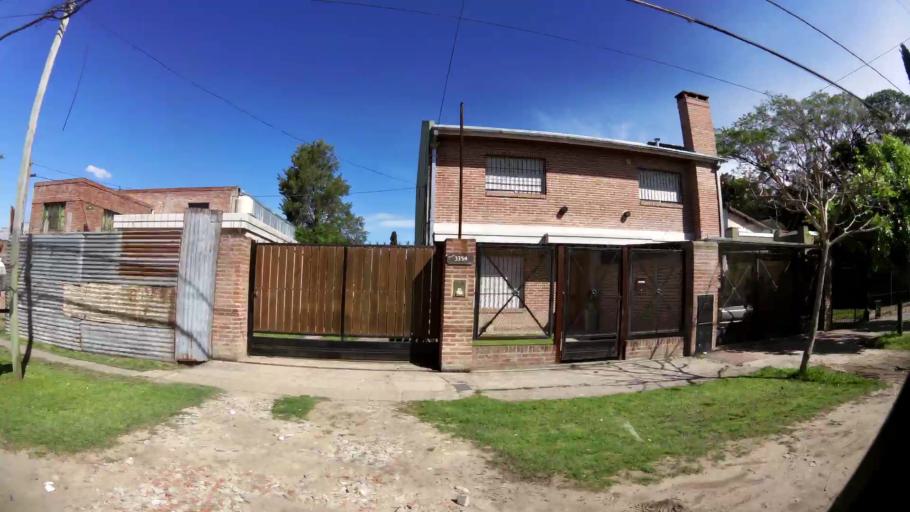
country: AR
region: Buenos Aires
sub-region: Partido de Almirante Brown
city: Adrogue
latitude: -34.7996
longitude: -58.3540
